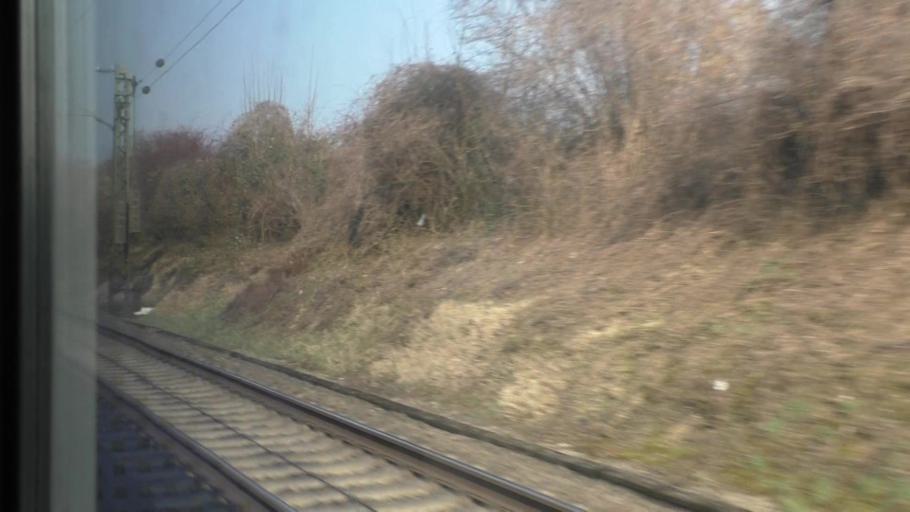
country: DE
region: Baden-Wuerttemberg
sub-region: Freiburg Region
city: Unterkrozingen
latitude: 47.9111
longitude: 7.6856
